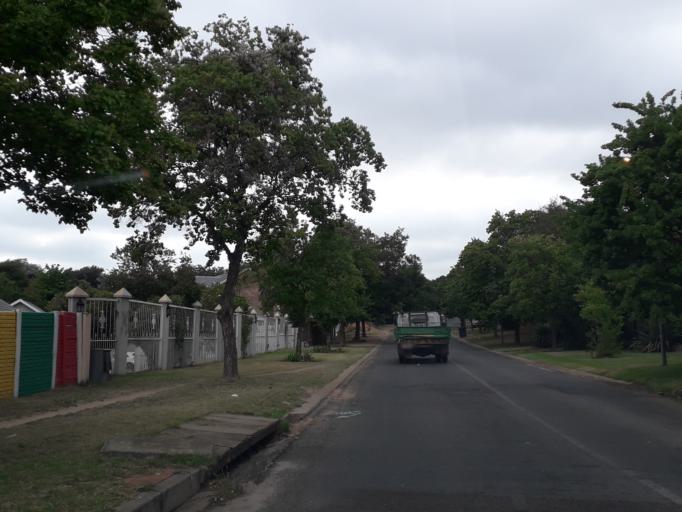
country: ZA
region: Gauteng
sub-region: City of Johannesburg Metropolitan Municipality
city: Roodepoort
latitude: -26.1061
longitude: 27.9449
